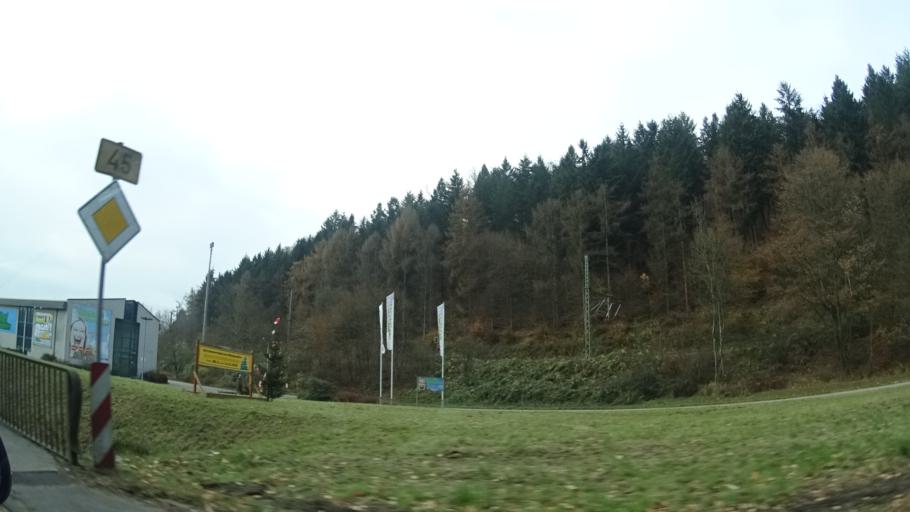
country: DE
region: Baden-Wuerttemberg
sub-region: Karlsruhe Region
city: Bammental
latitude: 49.3651
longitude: 8.7867
